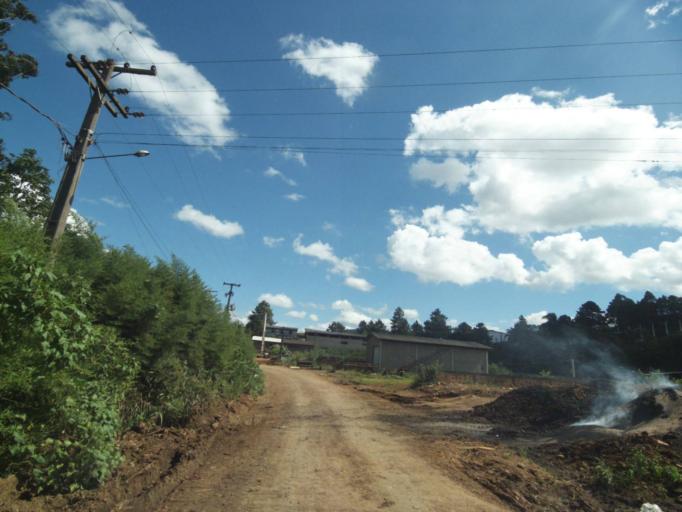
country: BR
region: Parana
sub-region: Uniao Da Vitoria
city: Uniao da Vitoria
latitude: -26.1510
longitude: -51.5387
